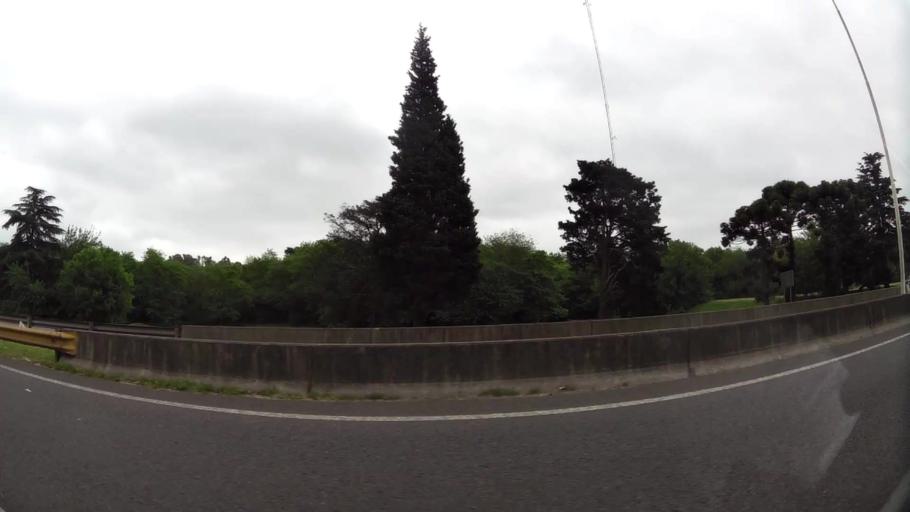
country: AR
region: Buenos Aires
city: San Justo
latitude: -34.7490
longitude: -58.5222
